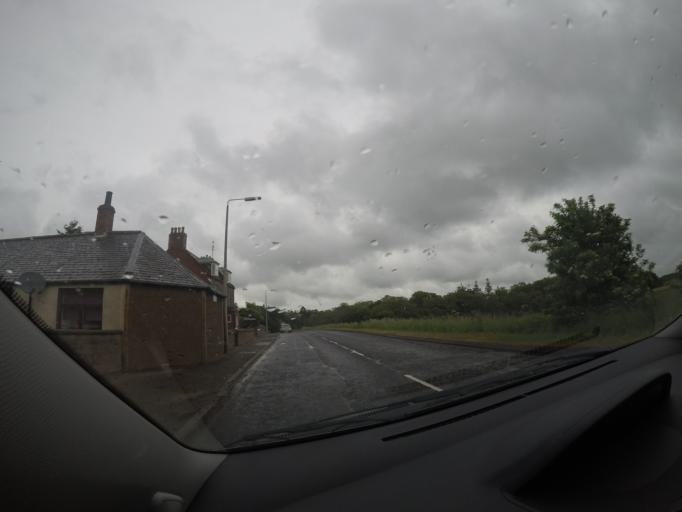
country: GB
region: Scotland
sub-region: Angus
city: Brechin
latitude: 56.7498
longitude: -2.6456
